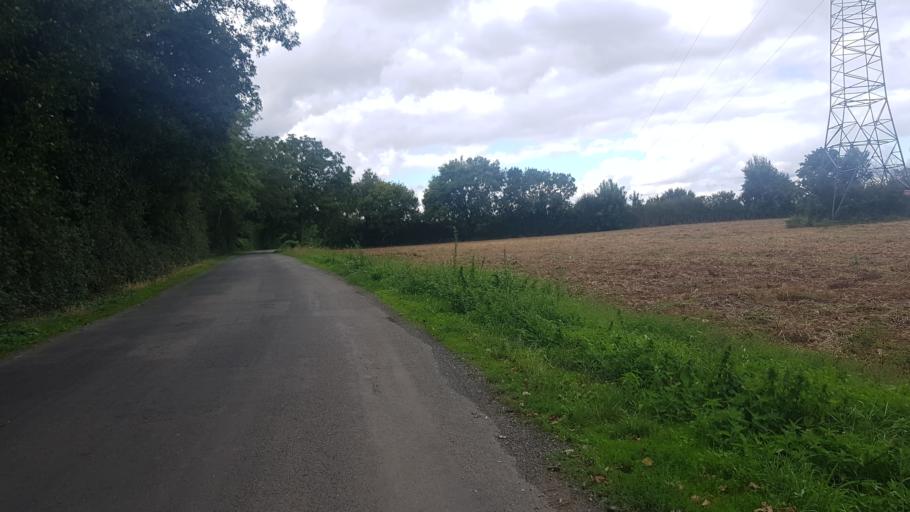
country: FR
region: Poitou-Charentes
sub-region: Departement des Deux-Sevres
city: Vouille
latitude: 46.3325
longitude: -0.3469
